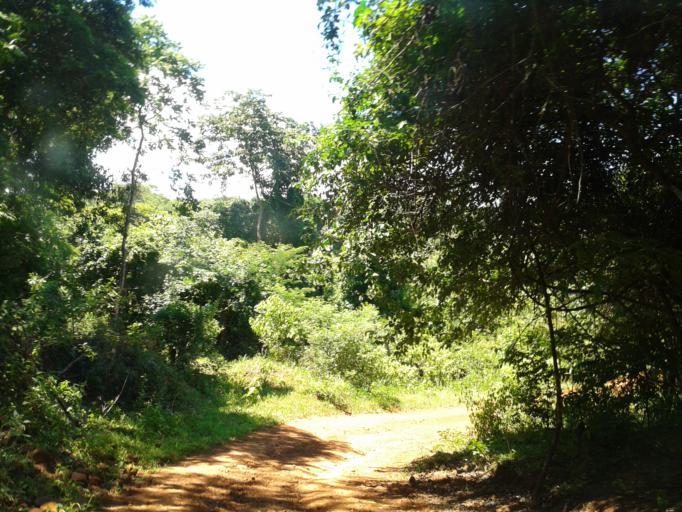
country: BR
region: Minas Gerais
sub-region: Centralina
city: Centralina
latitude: -18.6894
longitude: -49.1789
